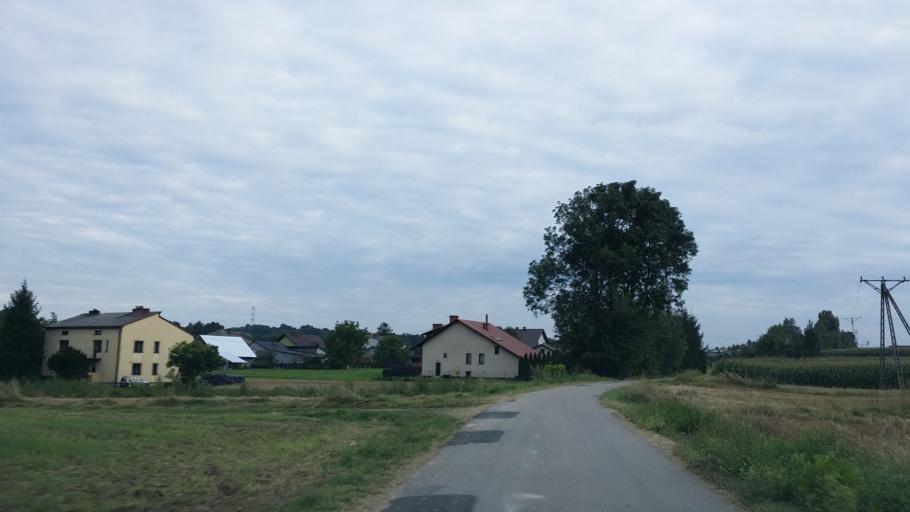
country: PL
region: Lesser Poland Voivodeship
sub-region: Powiat wadowicki
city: Spytkowice
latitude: 49.9927
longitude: 19.4994
